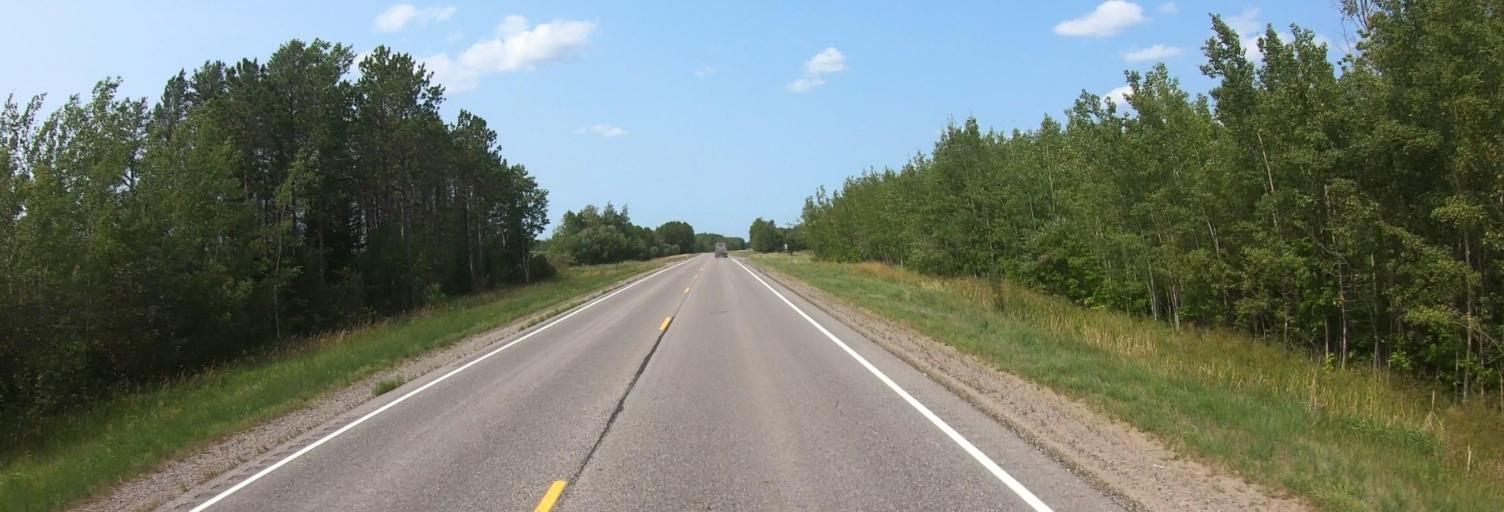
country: US
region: Minnesota
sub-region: Lake of the Woods County
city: Baudette
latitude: 48.6340
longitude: -94.1220
